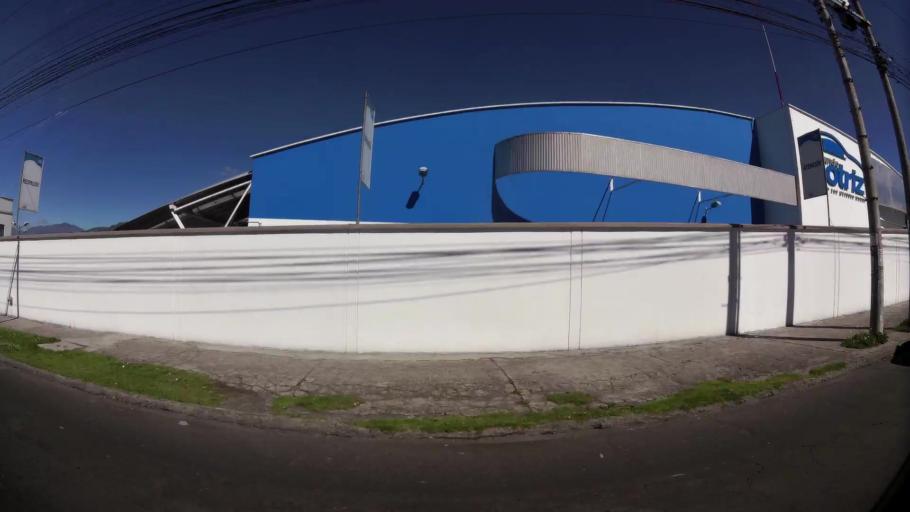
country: EC
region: Pichincha
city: Quito
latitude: -0.1326
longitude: -78.4709
